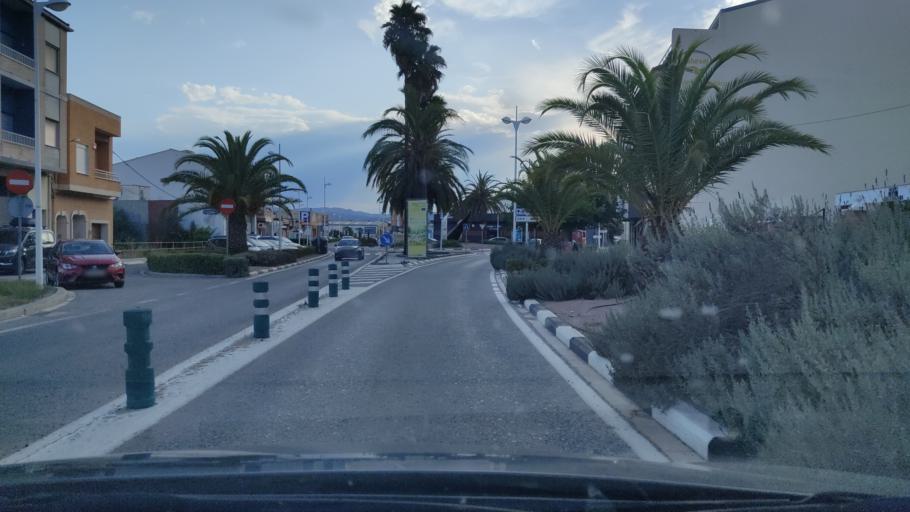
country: ES
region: Valencia
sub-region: Provincia de Valencia
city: Monserrat
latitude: 39.3577
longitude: -0.5962
